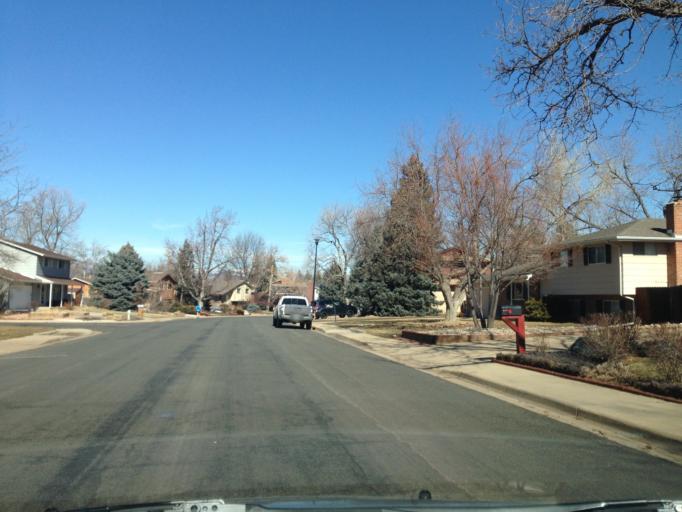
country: US
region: Colorado
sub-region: Boulder County
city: Boulder
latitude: 39.9904
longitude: -105.2284
